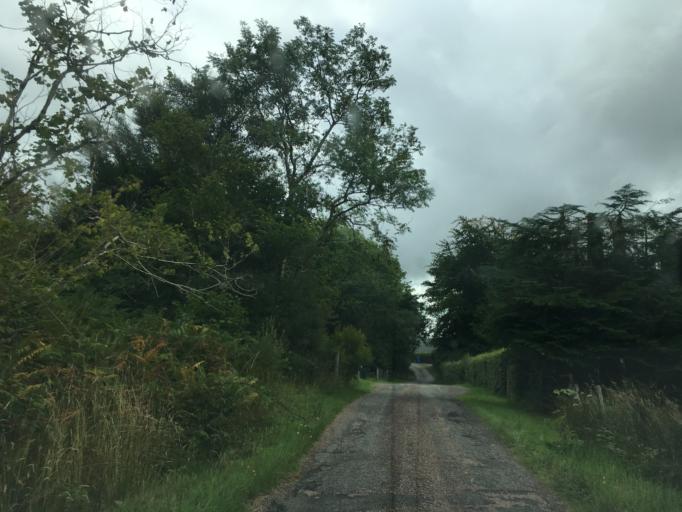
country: GB
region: Scotland
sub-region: Argyll and Bute
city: Oban
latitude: 56.2795
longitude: -5.3588
